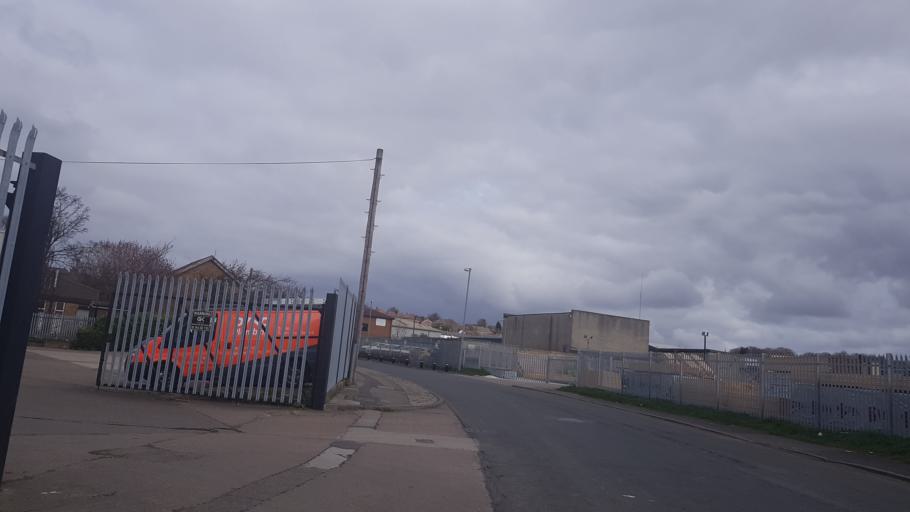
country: GB
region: England
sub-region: City and Borough of Wakefield
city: Castleford
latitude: 53.7143
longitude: -1.3406
